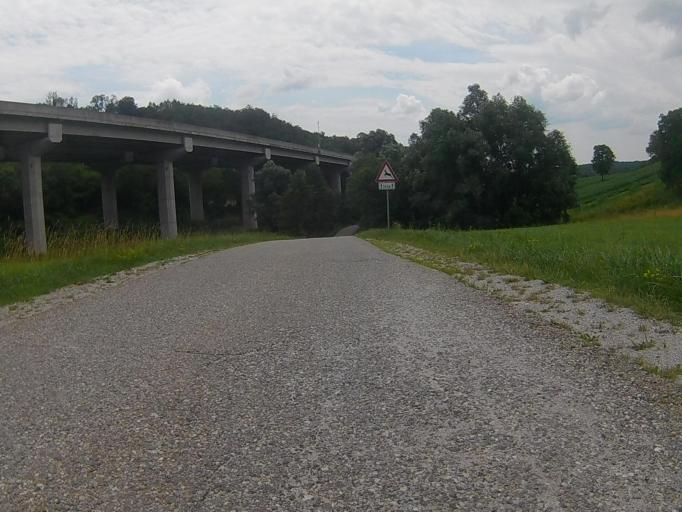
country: SI
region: Sentilj
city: Sentilj v Slov. Goricah
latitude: 46.6622
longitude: 15.6450
